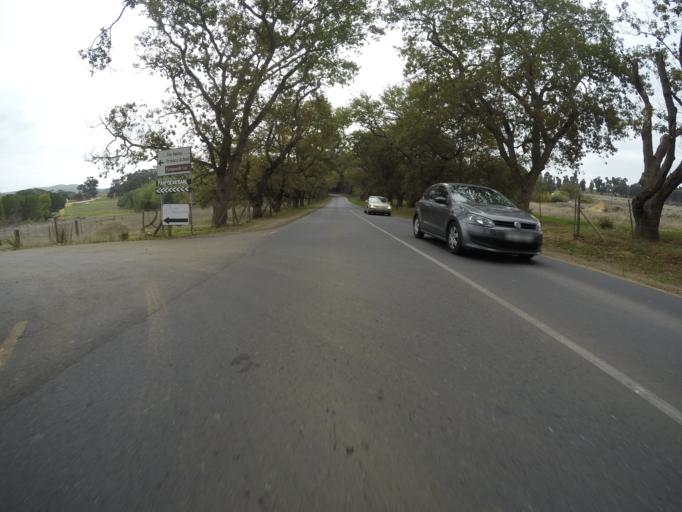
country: ZA
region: Western Cape
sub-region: City of Cape Town
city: Kraaifontein
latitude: -33.8476
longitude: 18.6281
